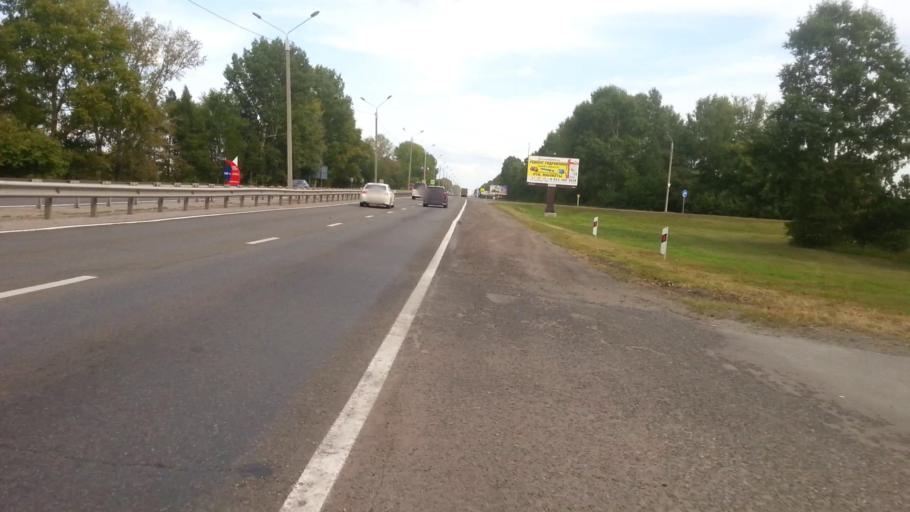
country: RU
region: Altai Krai
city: Vlasikha
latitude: 53.3534
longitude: 83.5554
